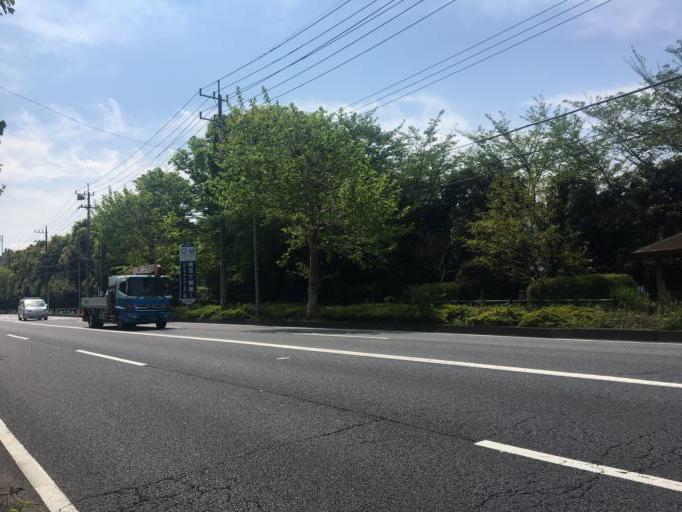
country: JP
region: Saitama
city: Wako
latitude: 35.7804
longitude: 139.6157
